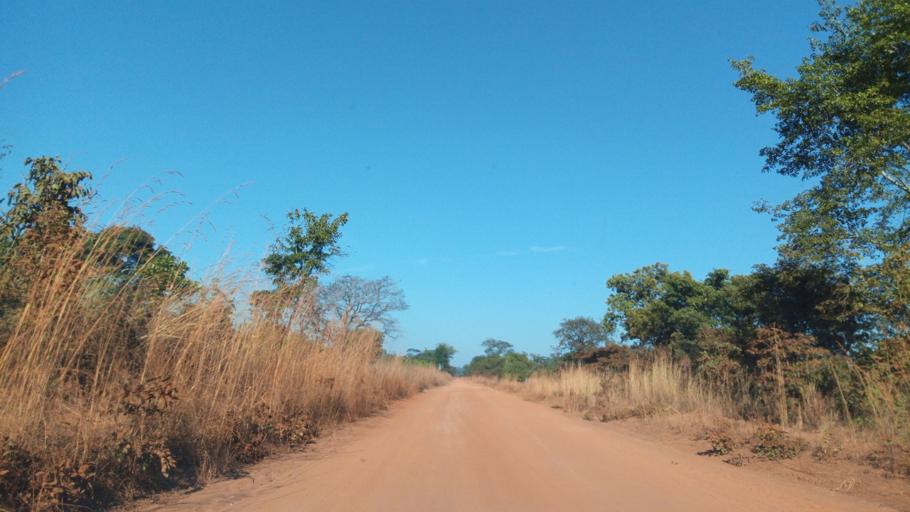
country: ZM
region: Luapula
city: Mwense
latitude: -10.6014
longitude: 28.4239
